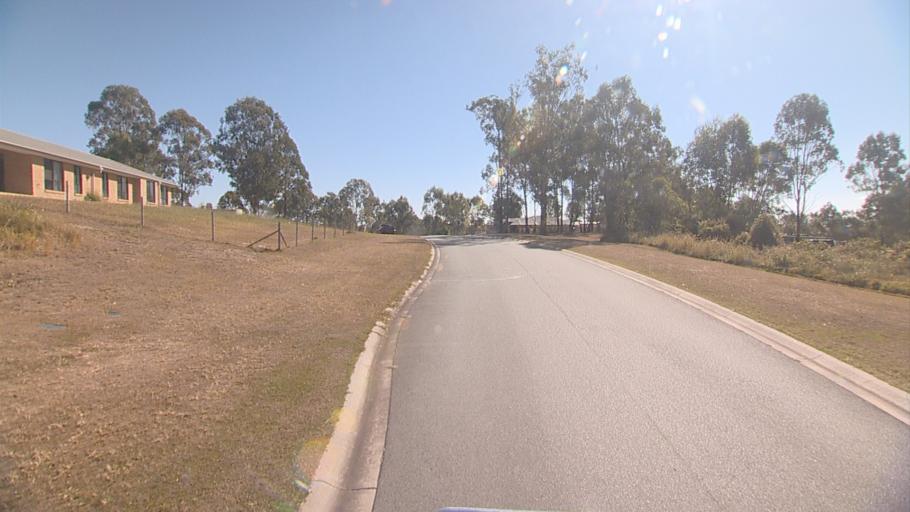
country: AU
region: Queensland
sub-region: Logan
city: Cedar Vale
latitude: -27.8697
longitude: 153.0352
